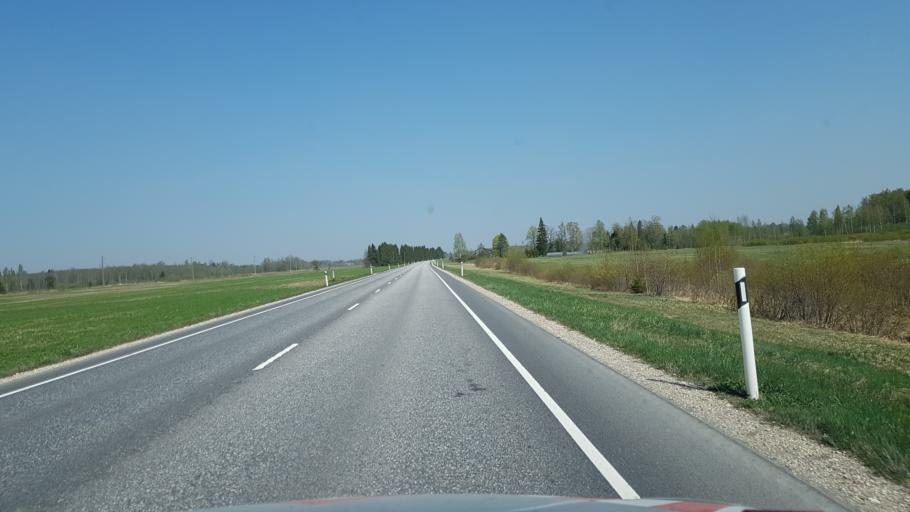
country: EE
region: Paernumaa
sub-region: Tootsi vald
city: Tootsi
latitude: 58.6017
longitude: 24.9112
